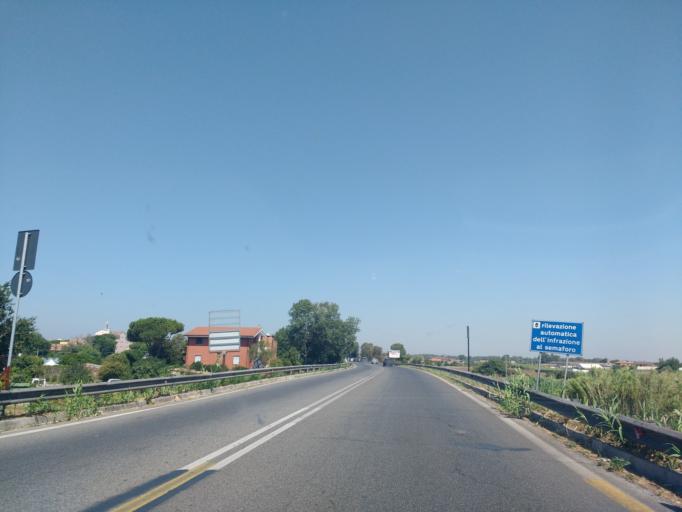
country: IT
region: Latium
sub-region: Citta metropolitana di Roma Capitale
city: Lido di Ostia
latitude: 41.7548
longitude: 12.2775
